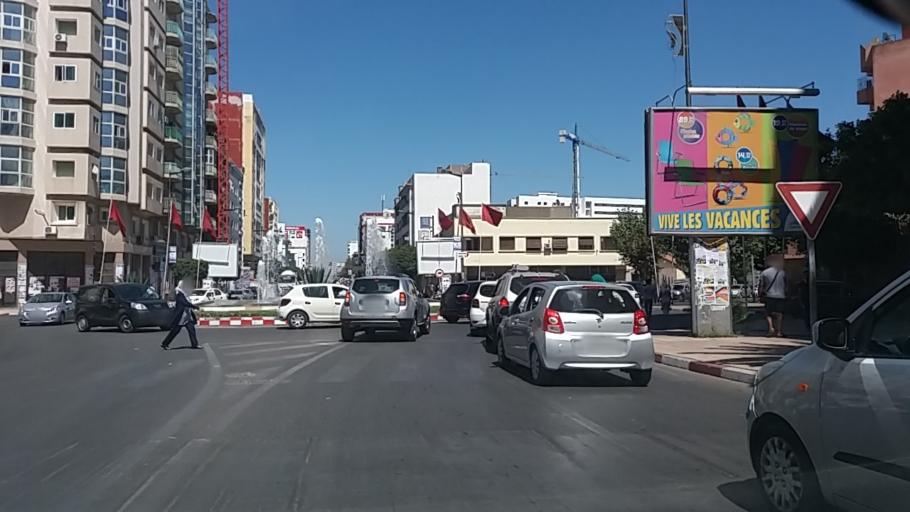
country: MA
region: Gharb-Chrarda-Beni Hssen
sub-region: Kenitra Province
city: Kenitra
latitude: 34.2585
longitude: -6.5875
